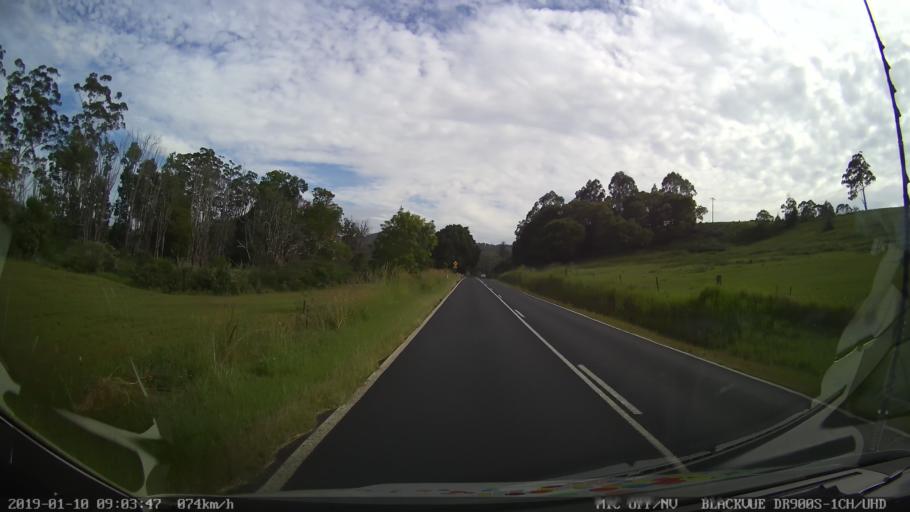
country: AU
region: New South Wales
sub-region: Coffs Harbour
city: Coffs Harbour
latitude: -30.2611
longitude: 153.0495
